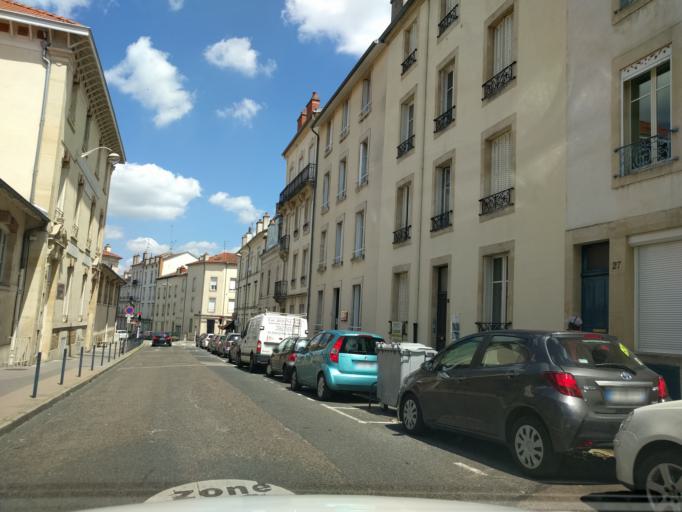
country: FR
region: Lorraine
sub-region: Departement de Meurthe-et-Moselle
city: Nancy
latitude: 48.6825
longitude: 6.1715
